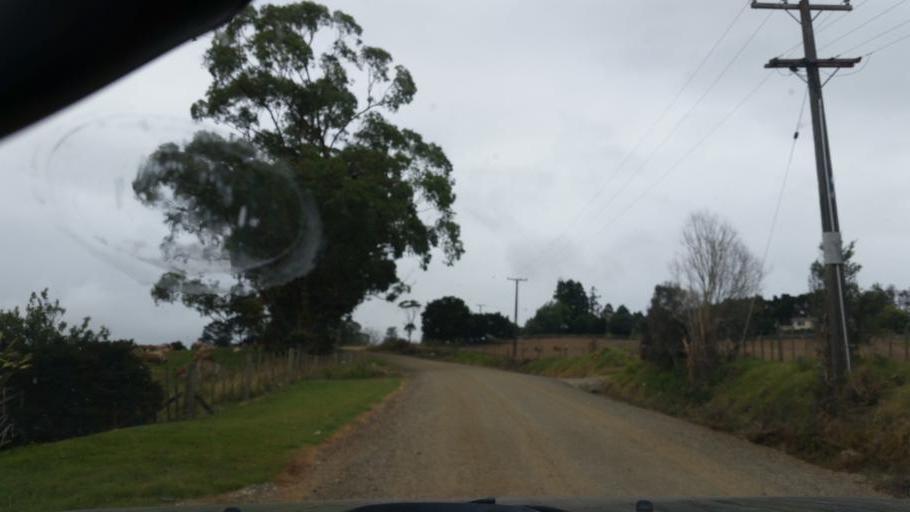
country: NZ
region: Auckland
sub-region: Auckland
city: Wellsford
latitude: -36.1650
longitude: 174.4379
